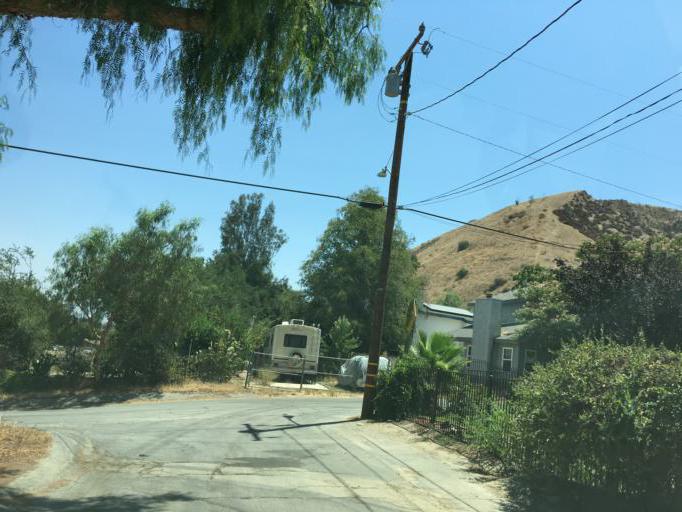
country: US
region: California
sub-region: Los Angeles County
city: Val Verde
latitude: 34.4476
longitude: -118.6713
